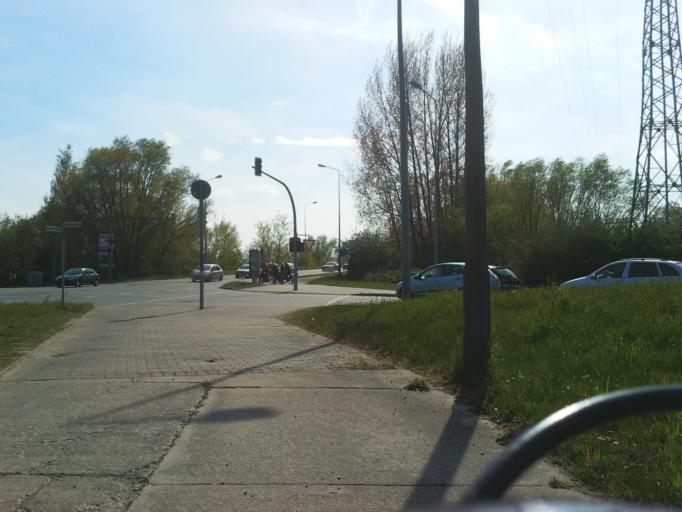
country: DE
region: Mecklenburg-Vorpommern
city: Warnemuende
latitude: 54.1195
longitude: 12.0764
